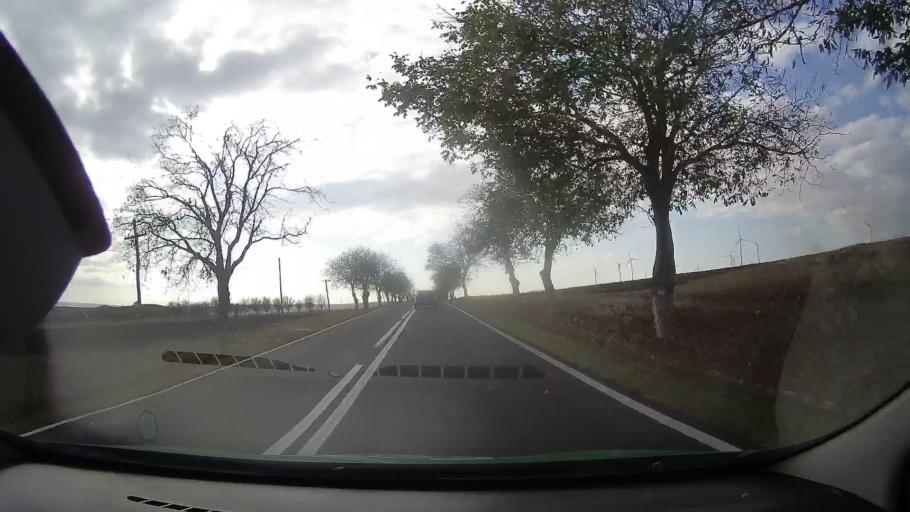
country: RO
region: Tulcea
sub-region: Comuna Topolog
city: Topolog
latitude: 44.8875
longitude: 28.3888
